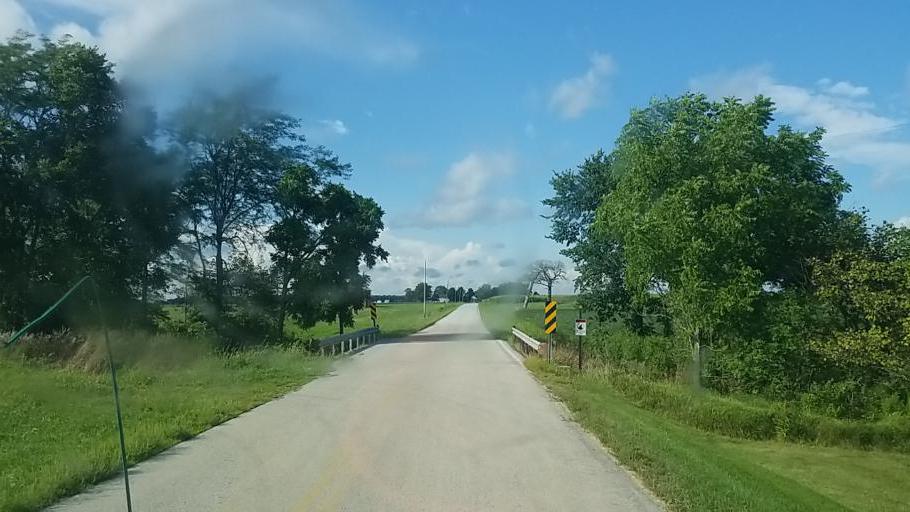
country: US
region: Ohio
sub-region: Hardin County
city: Forest
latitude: 40.7305
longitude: -83.5160
